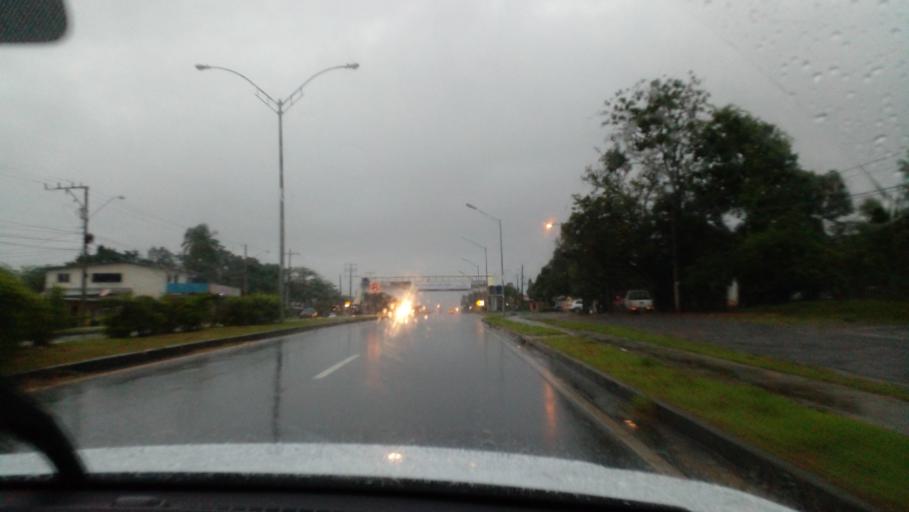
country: PA
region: Chiriqui
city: Las Lomas
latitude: 8.4282
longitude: -82.3912
